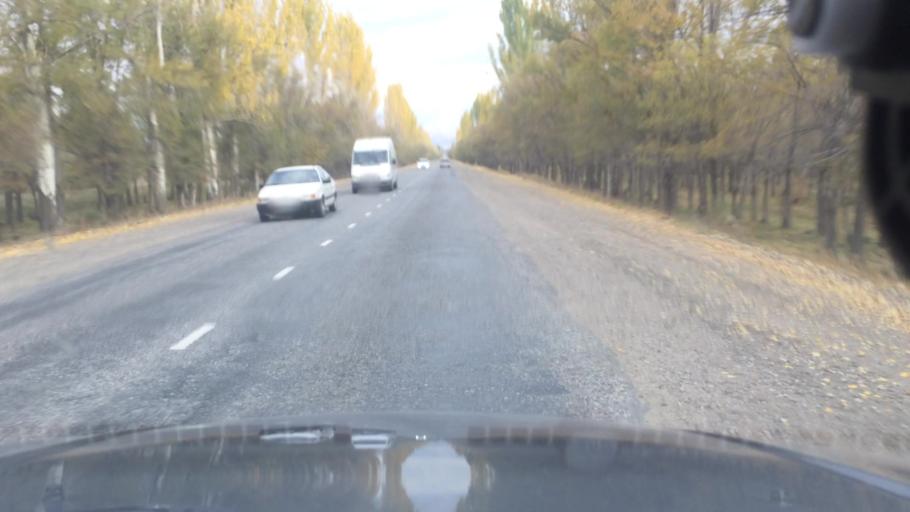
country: KG
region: Ysyk-Koel
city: Tyup
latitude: 42.6349
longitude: 78.3593
